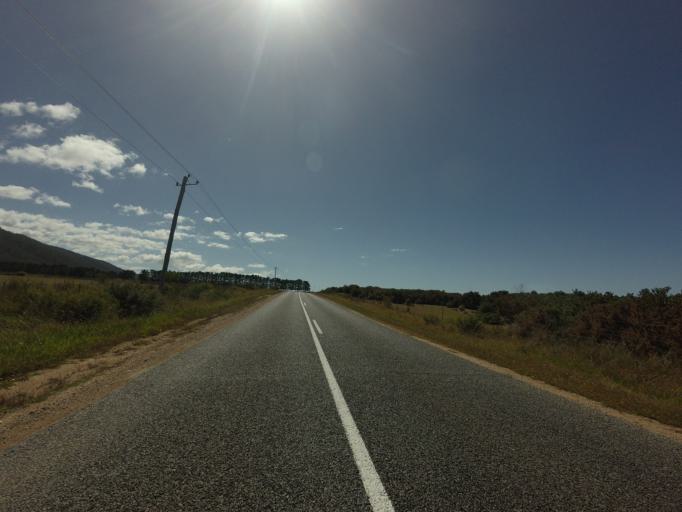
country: AU
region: Tasmania
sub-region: Break O'Day
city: St Helens
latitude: -41.7590
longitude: 148.2734
